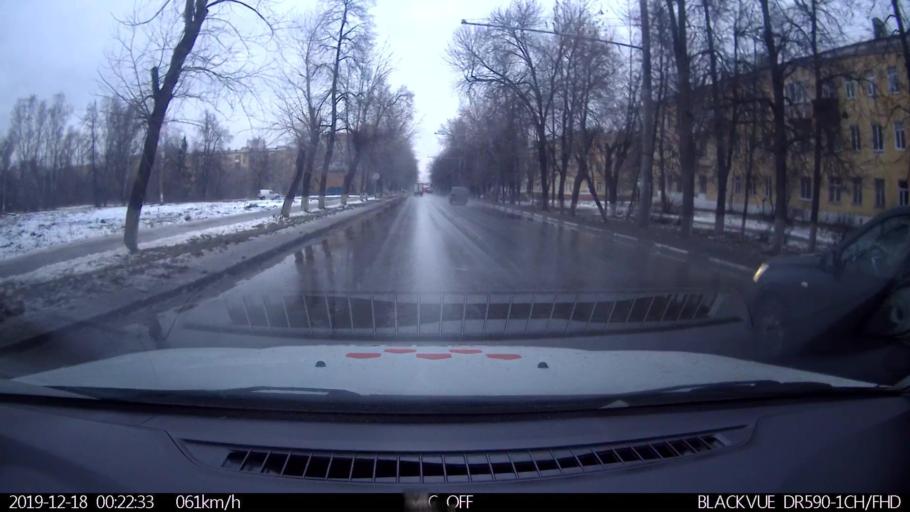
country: RU
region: Nizjnij Novgorod
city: Nizhniy Novgorod
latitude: 56.3328
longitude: 43.8851
